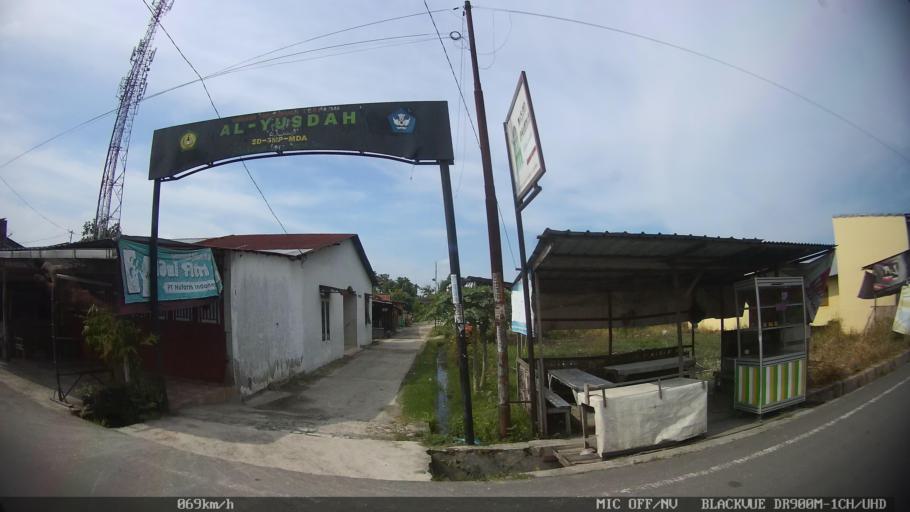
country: ID
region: North Sumatra
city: Percut
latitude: 3.6116
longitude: 98.8166
